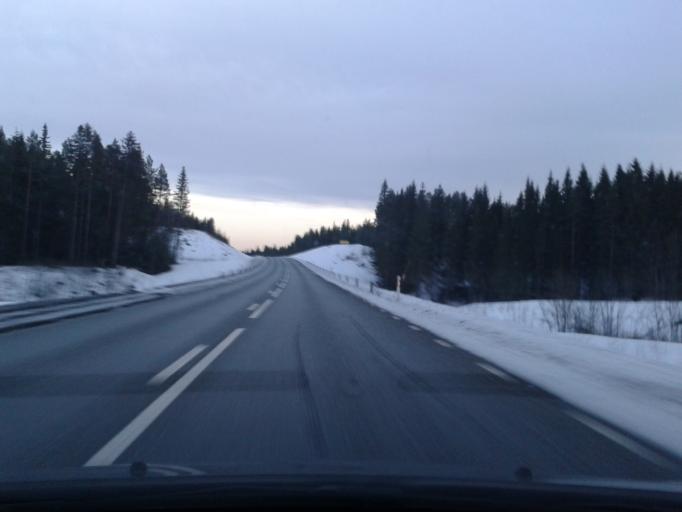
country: SE
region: Vaesternorrland
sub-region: Kramfors Kommun
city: Bollstabruk
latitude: 63.0471
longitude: 17.6270
